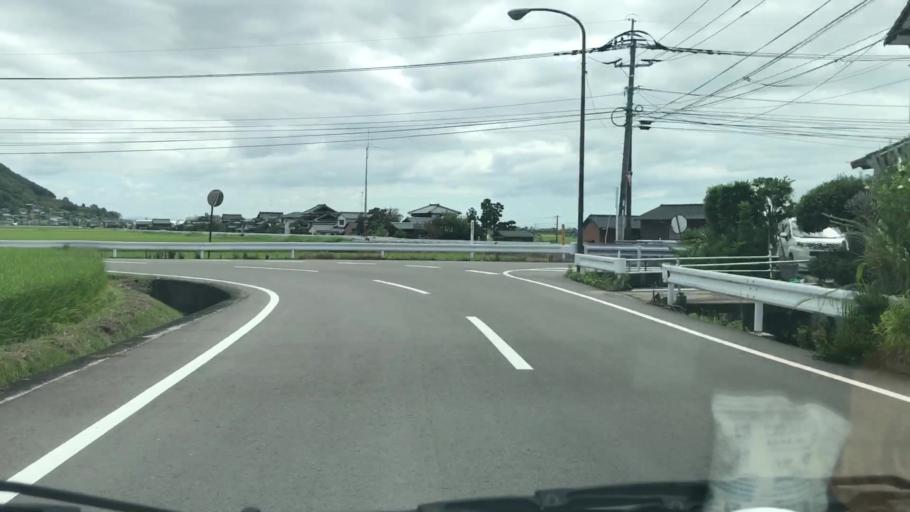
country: JP
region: Saga Prefecture
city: Takeocho-takeo
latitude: 33.2294
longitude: 130.1450
